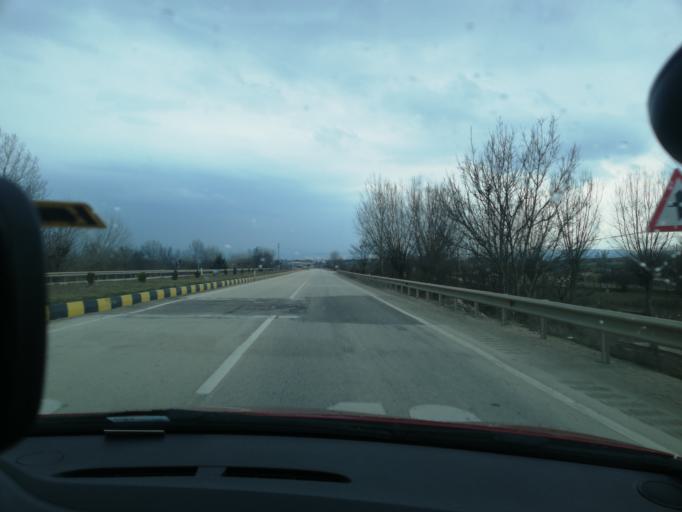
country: TR
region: Kastamonu
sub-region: Cide
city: Kastamonu
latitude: 41.4868
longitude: 33.7630
